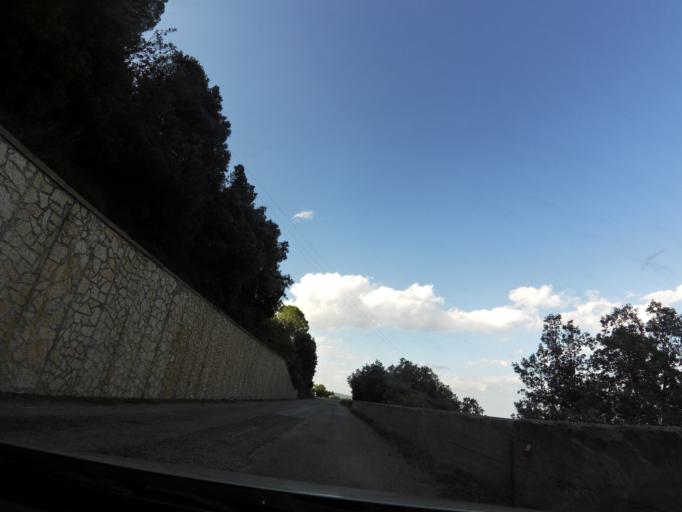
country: IT
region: Calabria
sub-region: Provincia di Reggio Calabria
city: Pazzano
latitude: 38.4664
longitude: 16.4241
